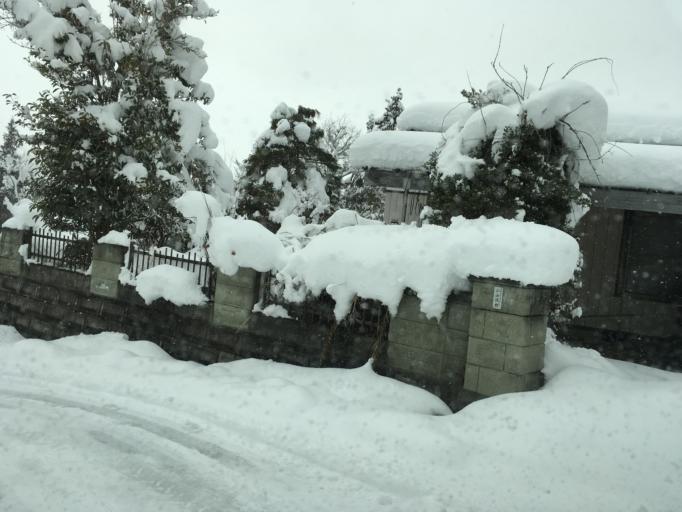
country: JP
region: Iwate
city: Ichinoseki
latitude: 38.9024
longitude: 141.1357
